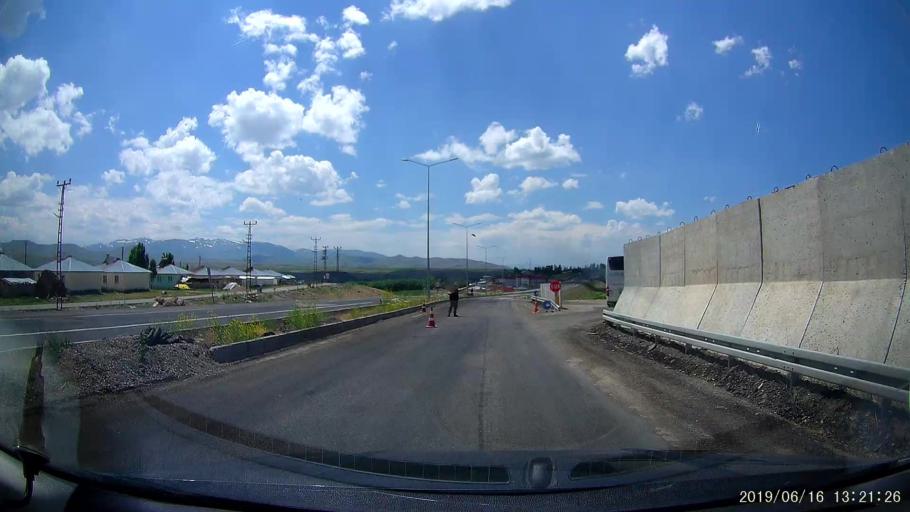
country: TR
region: Agri
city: Taslicay
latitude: 39.6326
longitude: 43.3939
